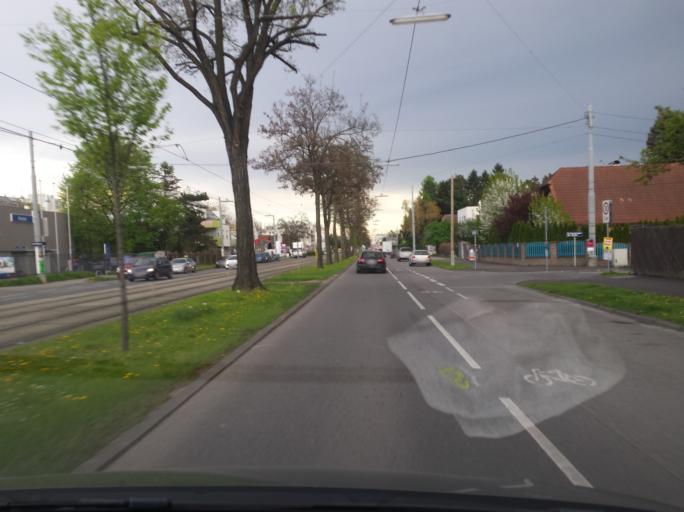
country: AT
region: Lower Austria
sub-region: Politischer Bezirk Wien-Umgebung
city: Gerasdorf bei Wien
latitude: 48.2377
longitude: 16.4339
